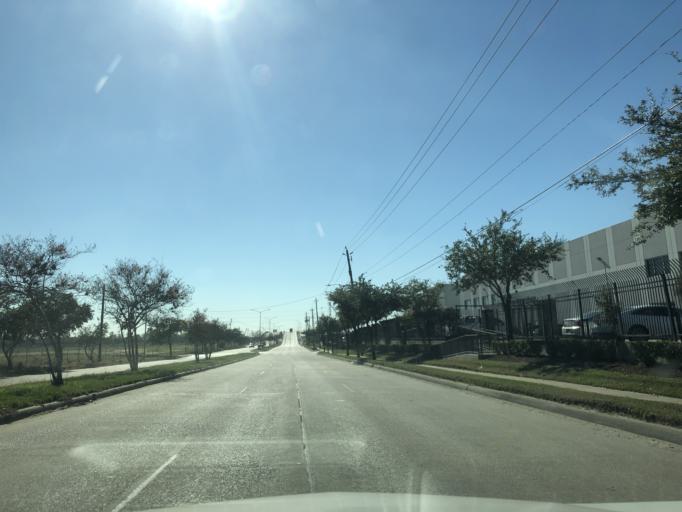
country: US
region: Texas
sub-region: Harris County
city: Houston
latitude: 29.8163
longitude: -95.3020
